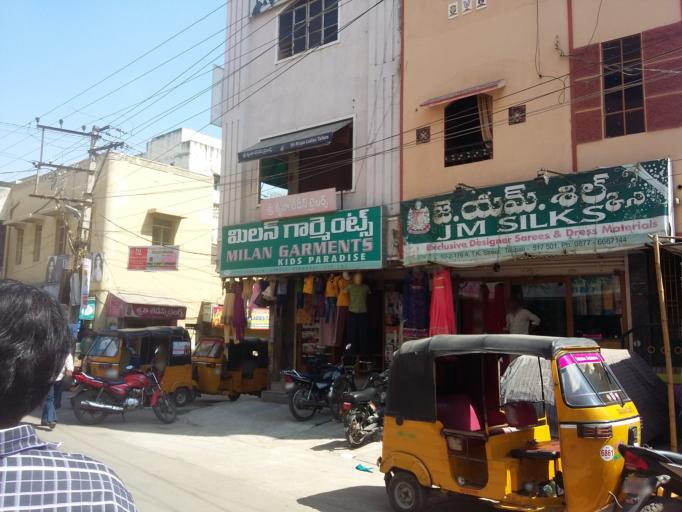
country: IN
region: Andhra Pradesh
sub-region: Chittoor
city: Tirupati
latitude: 13.6322
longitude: 79.4181
